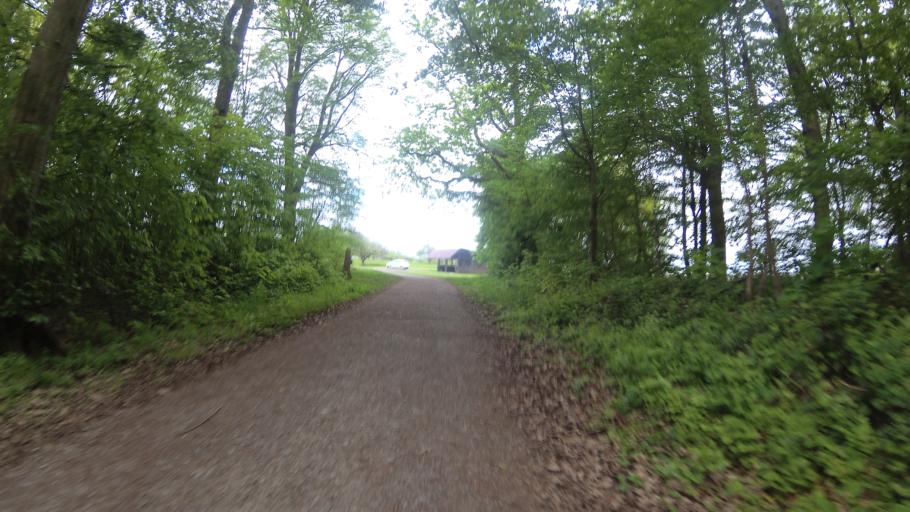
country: DE
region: Baden-Wuerttemberg
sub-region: Regierungsbezirk Stuttgart
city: Erlenbach
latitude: 49.1927
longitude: 9.2669
